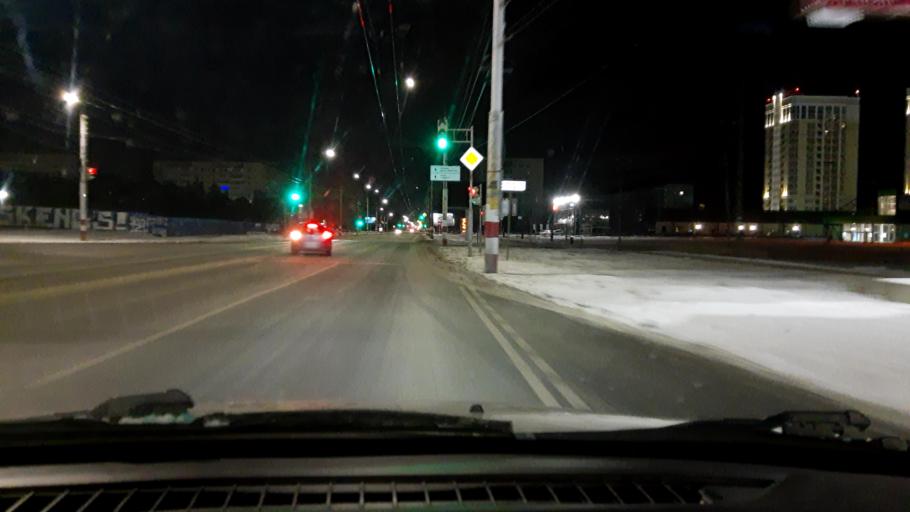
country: RU
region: Nizjnij Novgorod
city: Dzerzhinsk
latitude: 56.2279
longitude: 43.4129
